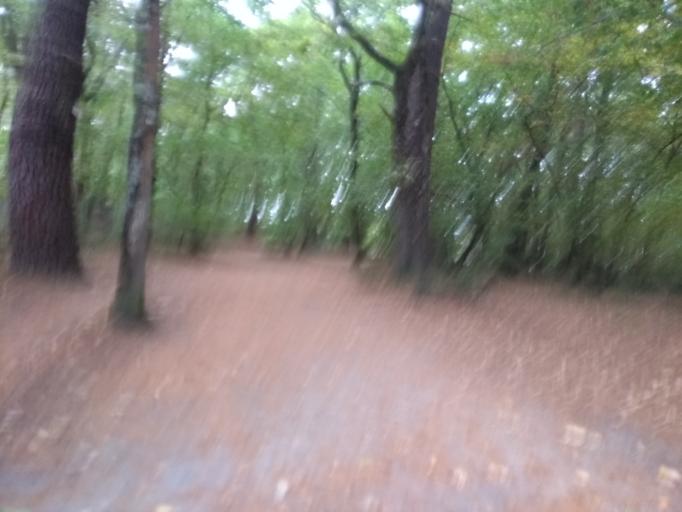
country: FR
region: Aquitaine
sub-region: Departement de la Gironde
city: Pessac
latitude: 44.8192
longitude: -0.6471
